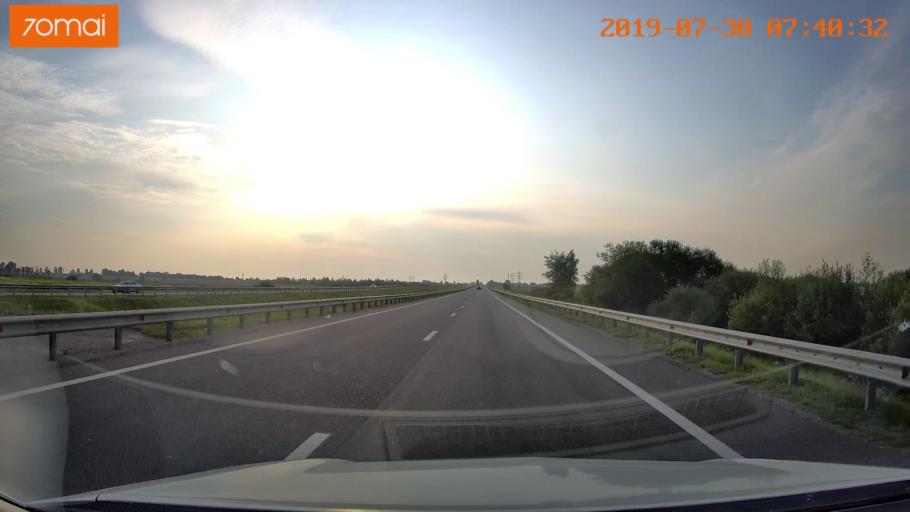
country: RU
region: Kaliningrad
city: Gvardeysk
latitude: 54.6486
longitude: 21.2265
